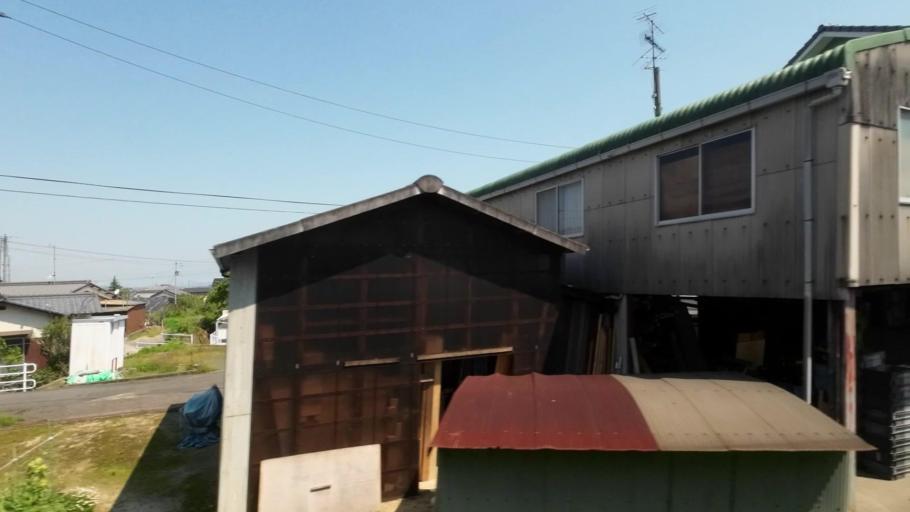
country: JP
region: Ehime
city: Saijo
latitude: 33.8972
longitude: 133.1233
